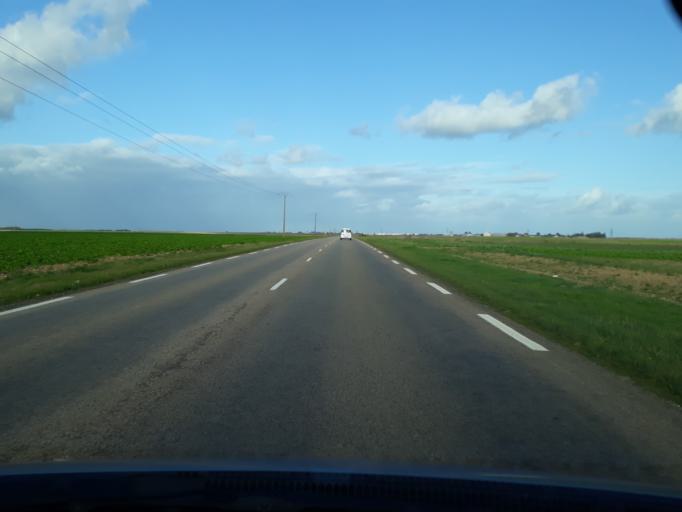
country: FR
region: Centre
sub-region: Departement du Loiret
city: Dadonville
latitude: 48.2171
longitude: 2.3035
